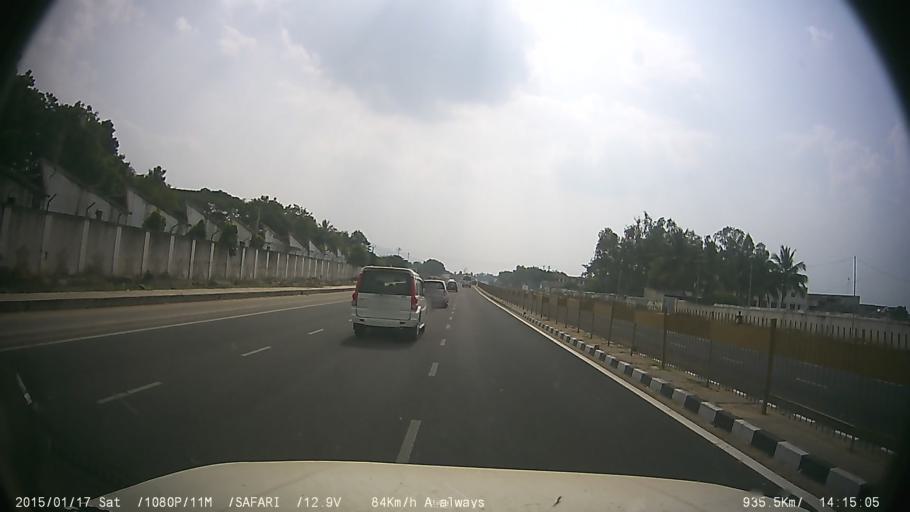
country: IN
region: Tamil Nadu
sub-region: Vellore
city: Ambur
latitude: 12.7693
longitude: 78.7093
